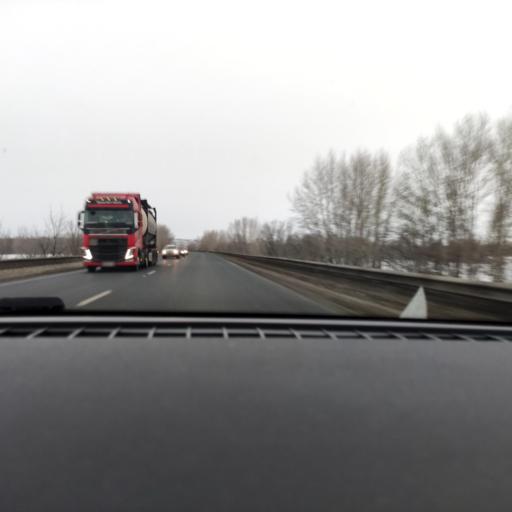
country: RU
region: Samara
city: Smyshlyayevka
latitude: 53.2135
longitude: 50.5046
